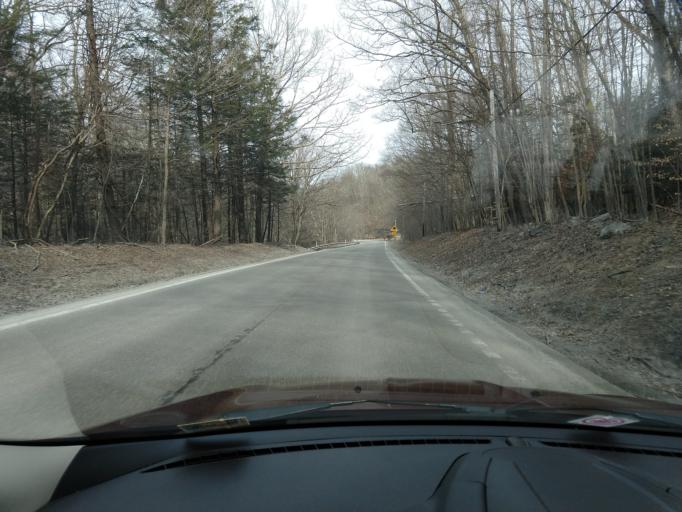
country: US
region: West Virginia
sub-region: Tucker County
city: Parsons
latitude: 38.9029
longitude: -79.4887
